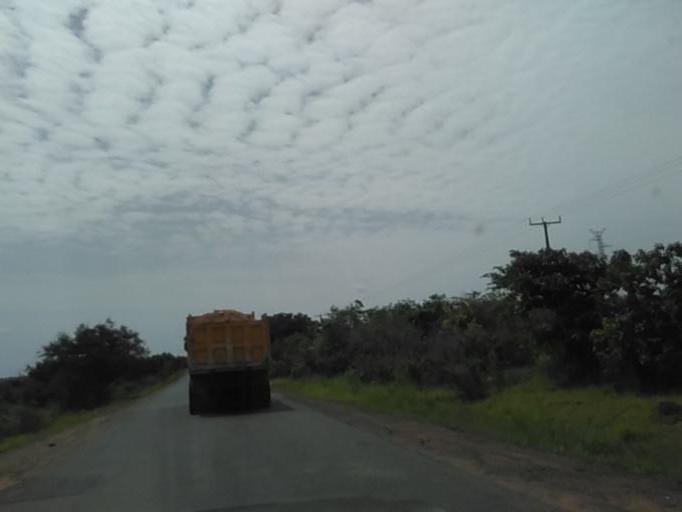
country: GH
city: Akropong
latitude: 6.0951
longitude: 0.0533
